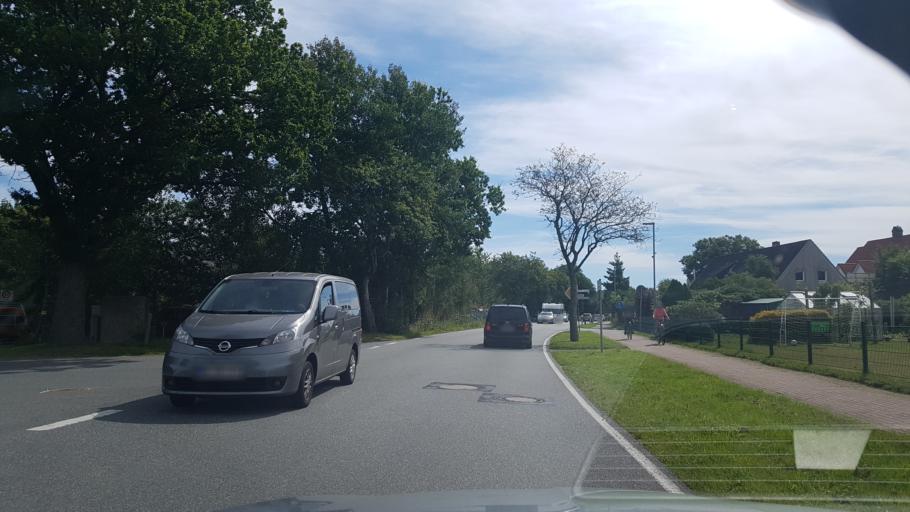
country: DE
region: Schleswig-Holstein
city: Handewitt
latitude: 54.7952
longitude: 9.3069
